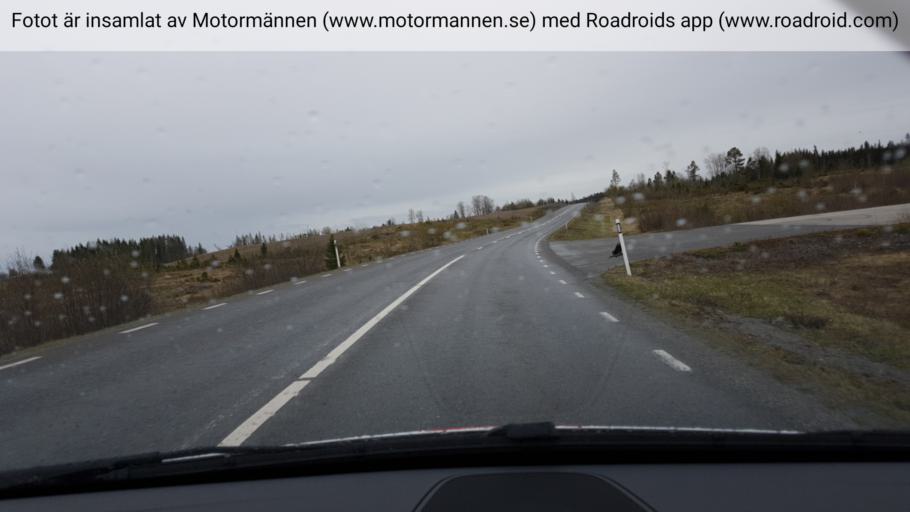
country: SE
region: Jaemtland
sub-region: OEstersunds Kommun
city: Ostersund
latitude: 63.1861
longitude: 14.5356
